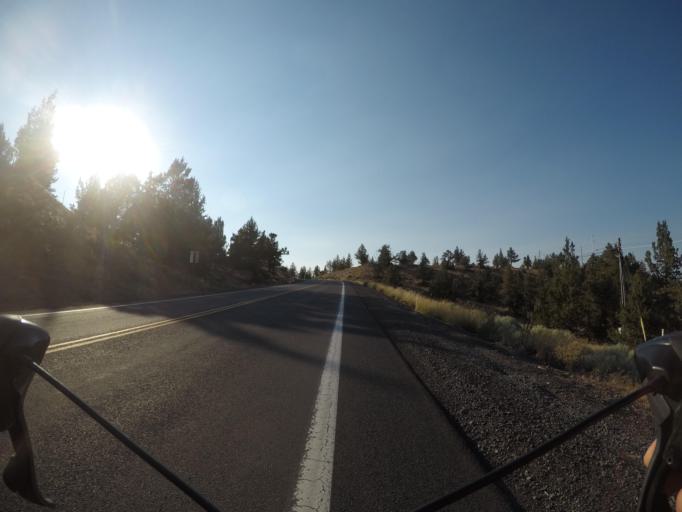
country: US
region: Oregon
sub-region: Deschutes County
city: Redmond
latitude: 44.2728
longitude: -121.2610
